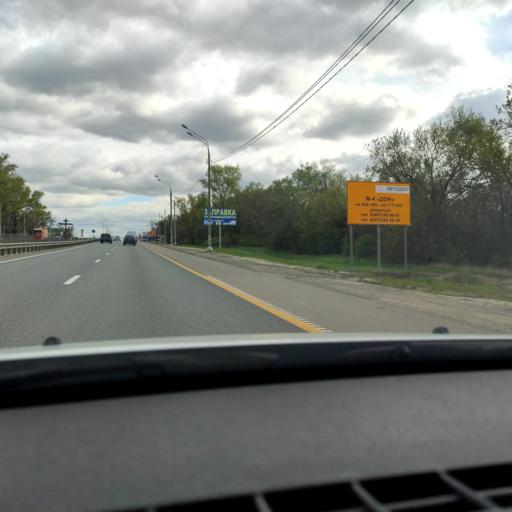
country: RU
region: Lipetsk
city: Khlevnoye
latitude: 52.0901
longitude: 39.1782
